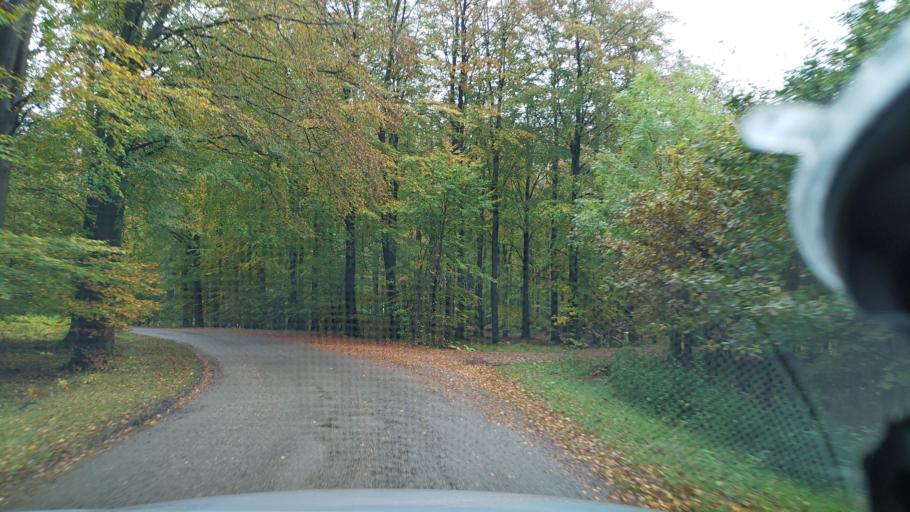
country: DK
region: Zealand
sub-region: Faxe Kommune
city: Ronnede
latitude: 55.2458
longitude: 11.9518
